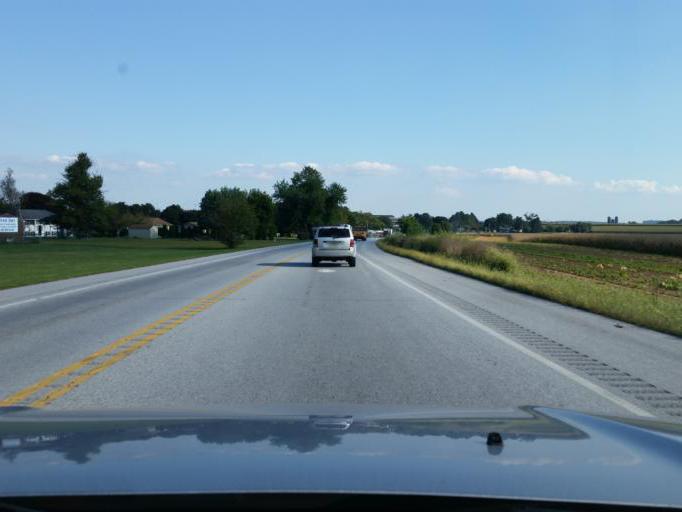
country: US
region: Pennsylvania
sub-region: Chester County
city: Atglen
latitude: 39.9337
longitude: -75.9541
